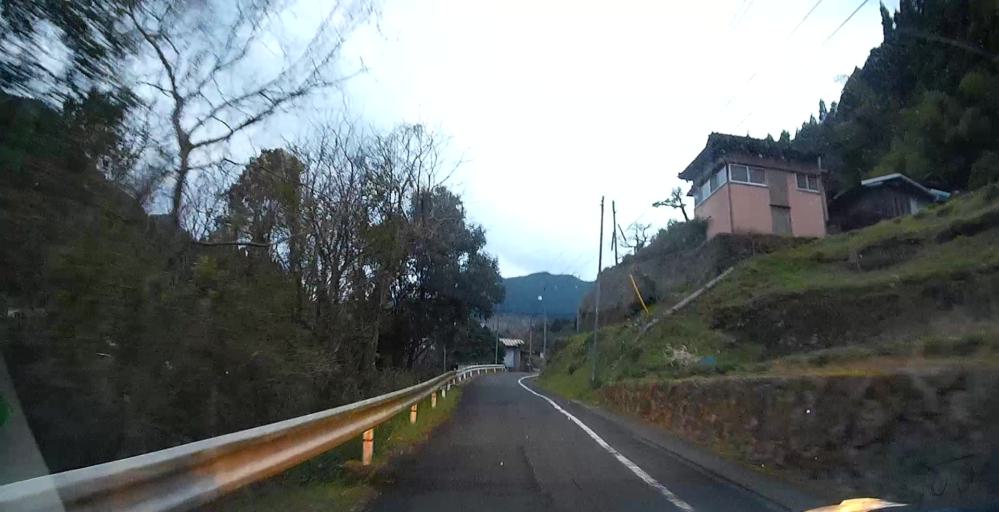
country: JP
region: Kumamoto
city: Minamata
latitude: 32.1525
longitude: 130.4411
